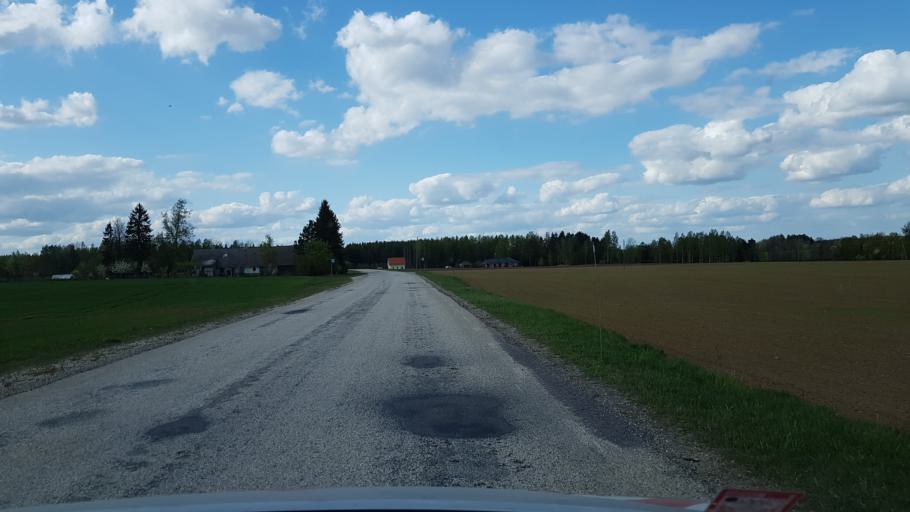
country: EE
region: Tartu
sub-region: UElenurme vald
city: Ulenurme
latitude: 58.2811
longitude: 26.9048
